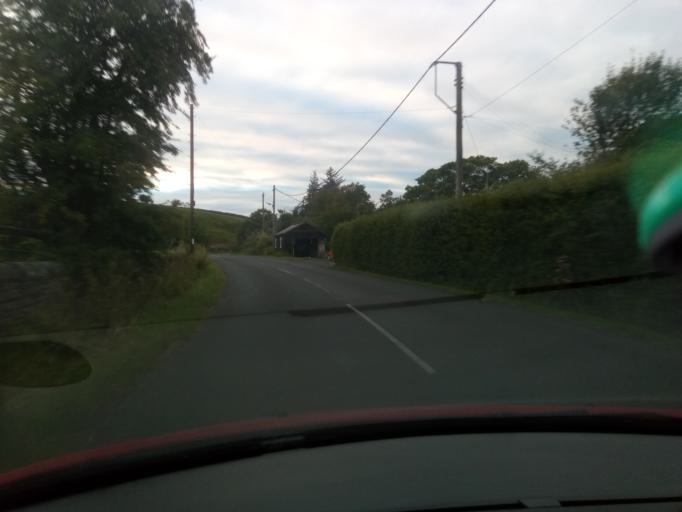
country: GB
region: England
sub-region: Northumberland
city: Bardon Mill
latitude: 54.9021
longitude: -2.2734
